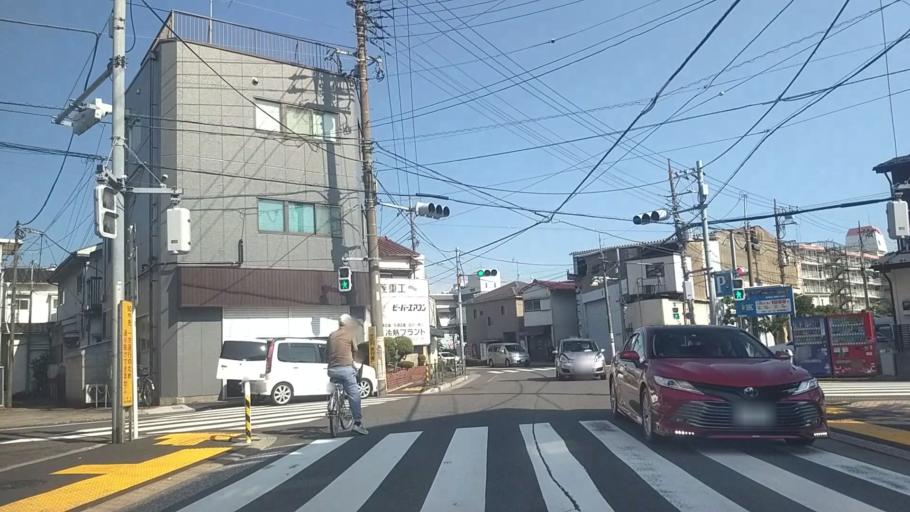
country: JP
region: Kanagawa
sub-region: Kawasaki-shi
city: Kawasaki
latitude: 35.5472
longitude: 139.7344
